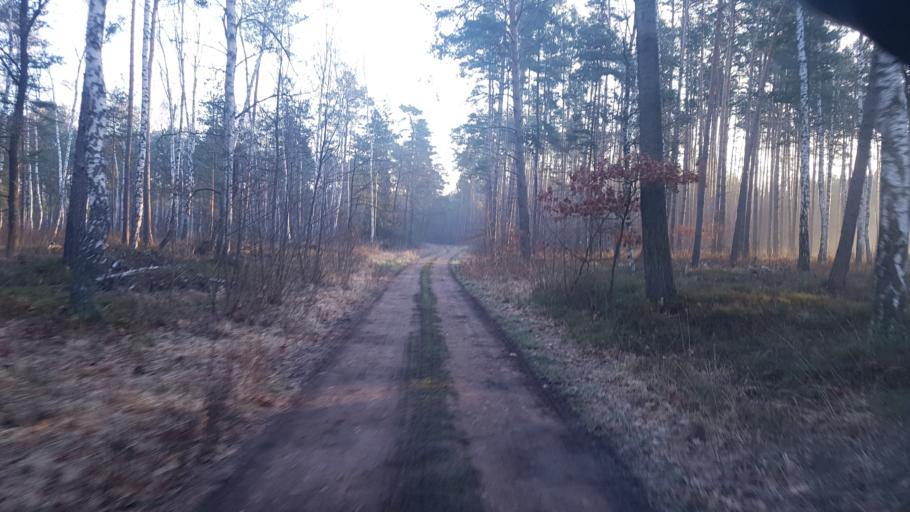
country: DE
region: Brandenburg
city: Finsterwalde
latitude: 51.6734
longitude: 13.7532
